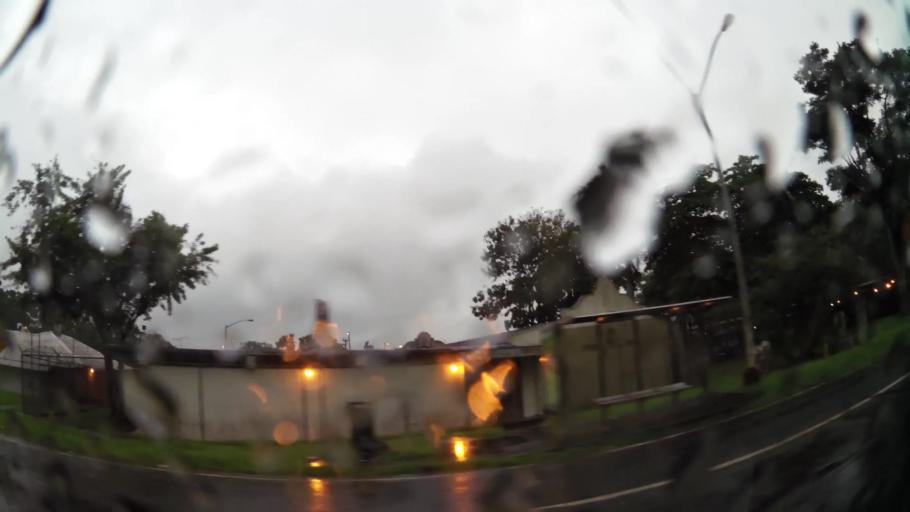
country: PA
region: Panama
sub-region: Distrito de Panama
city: Paraiso
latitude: 9.0250
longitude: -79.6187
